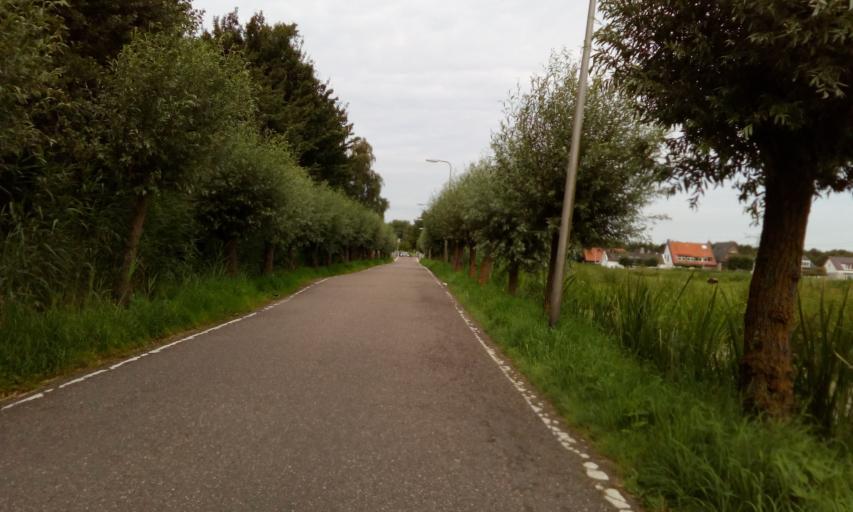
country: NL
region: South Holland
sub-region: Gemeente Capelle aan den IJssel
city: Capelle aan den IJssel
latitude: 51.9466
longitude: 4.6006
